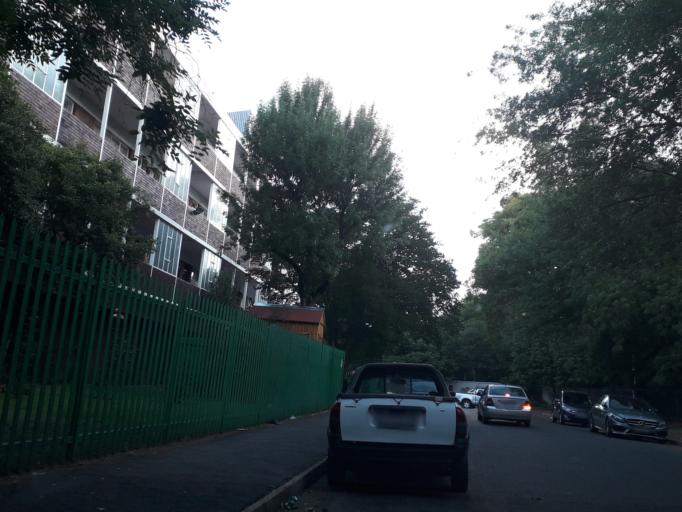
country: ZA
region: Gauteng
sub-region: City of Johannesburg Metropolitan Municipality
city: Johannesburg
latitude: -26.1356
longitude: 28.0503
